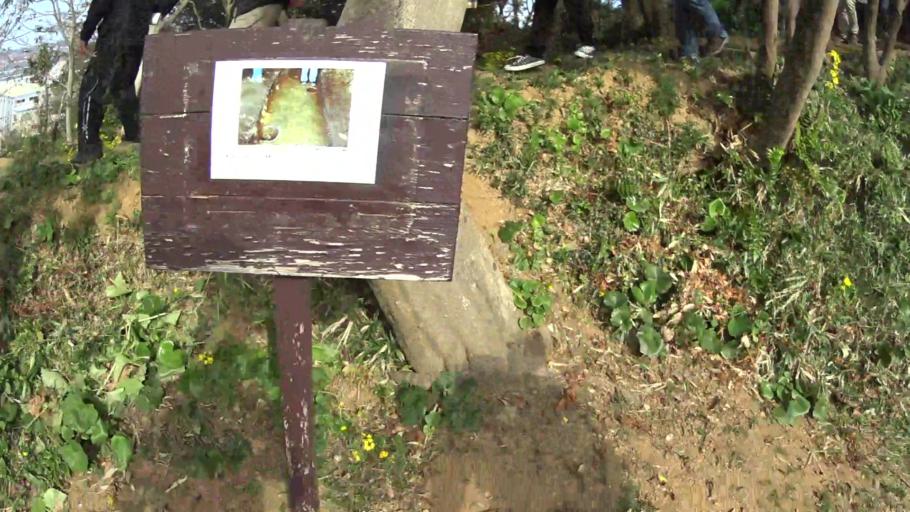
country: JP
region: Wakayama
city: Minato
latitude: 34.1935
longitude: 135.1401
